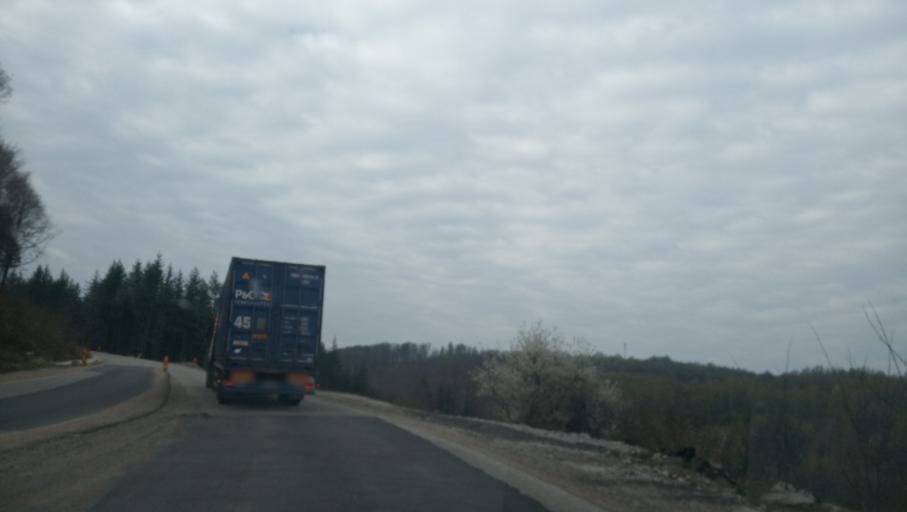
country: RO
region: Bihor
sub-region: Comuna Cristioru de Jos
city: Cristioru de Jos
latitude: 46.4140
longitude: 22.5366
